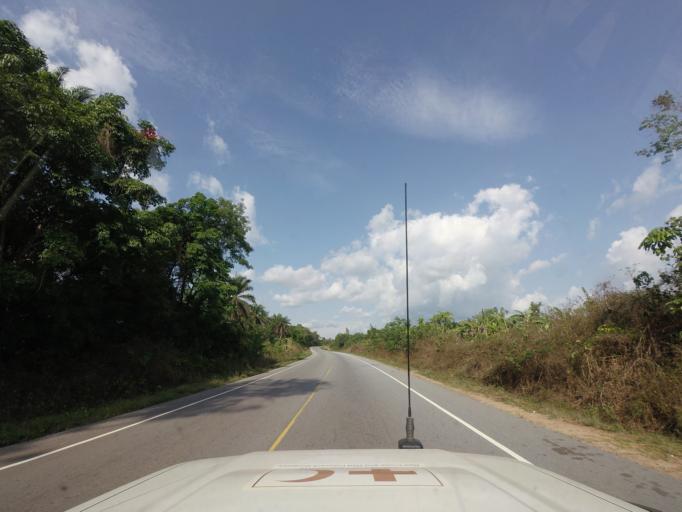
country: LR
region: Bong
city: Gbarnga
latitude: 6.8821
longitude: -9.7108
